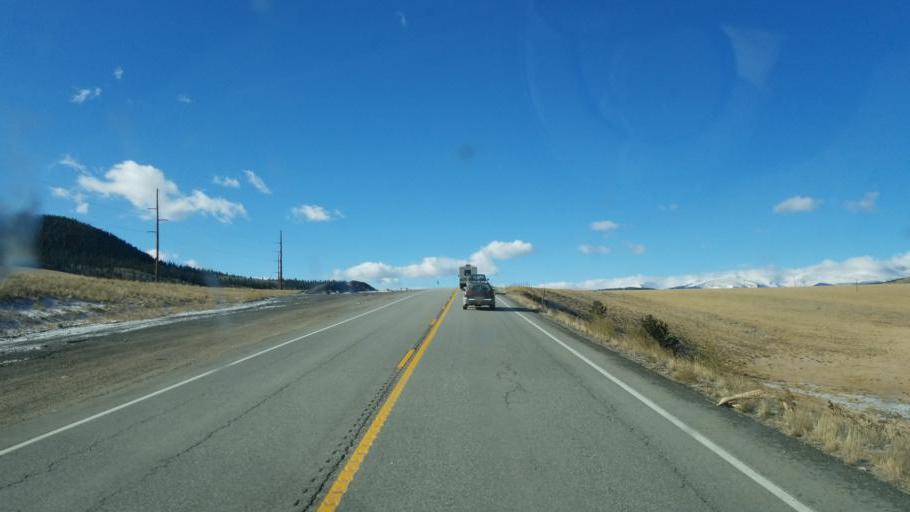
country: US
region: Colorado
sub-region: Park County
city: Fairplay
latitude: 39.2868
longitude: -105.9116
